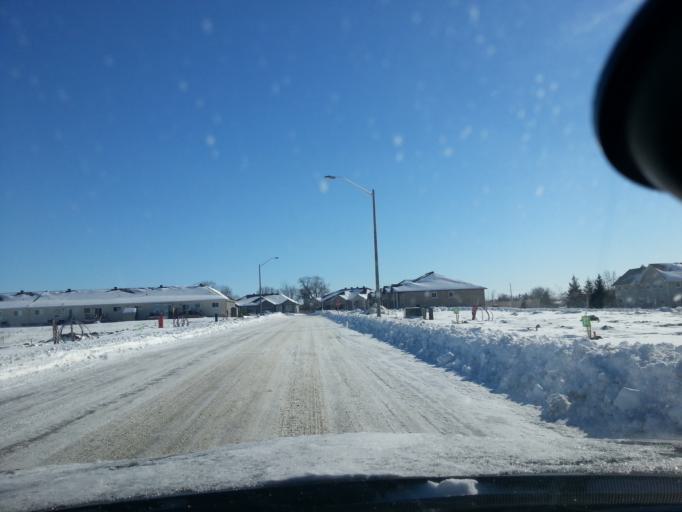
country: CA
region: Ontario
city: Carleton Place
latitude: 45.2357
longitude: -76.1884
